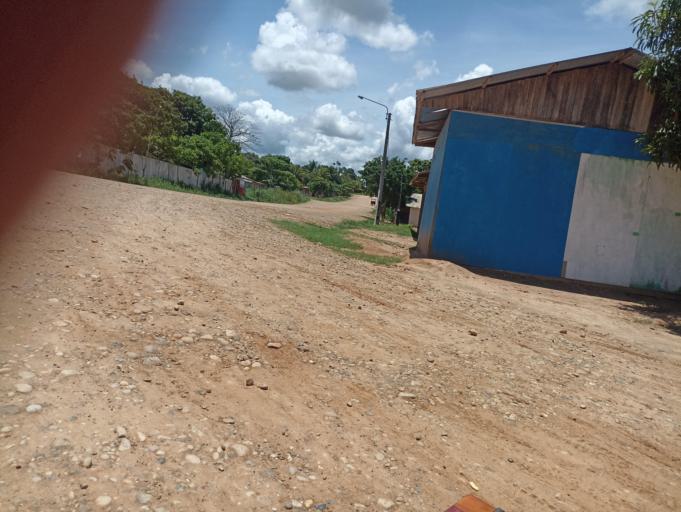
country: PE
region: Ucayali
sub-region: Provincia de Coronel Portillo
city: Puerto Callao
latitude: -8.3624
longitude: -74.5886
